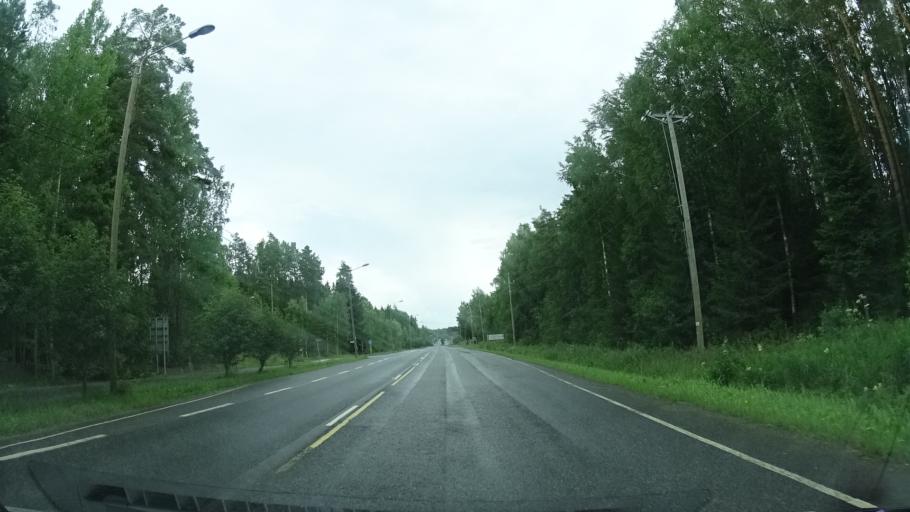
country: FI
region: Pirkanmaa
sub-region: Etelae-Pirkanmaa
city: Valkeakoski
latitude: 61.2740
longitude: 23.9747
